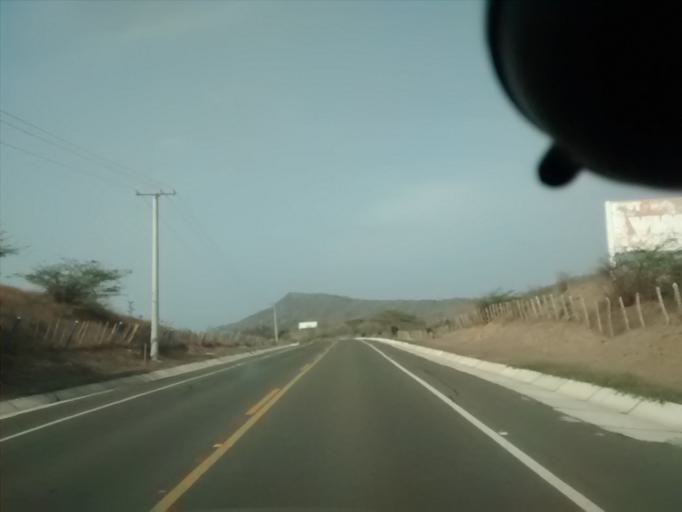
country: CO
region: Atlantico
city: Juan de Acosta
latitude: 10.8650
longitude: -75.0973
